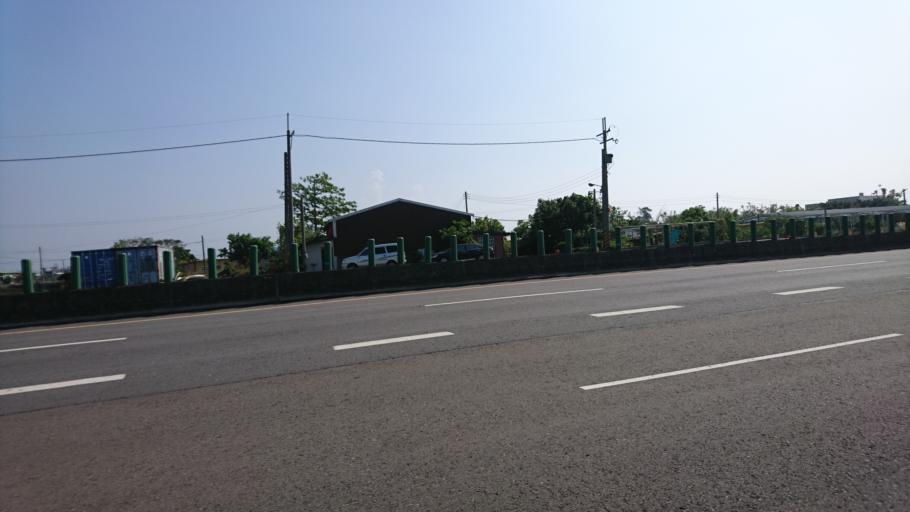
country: TW
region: Taiwan
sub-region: Miaoli
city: Miaoli
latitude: 24.6869
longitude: 120.8529
